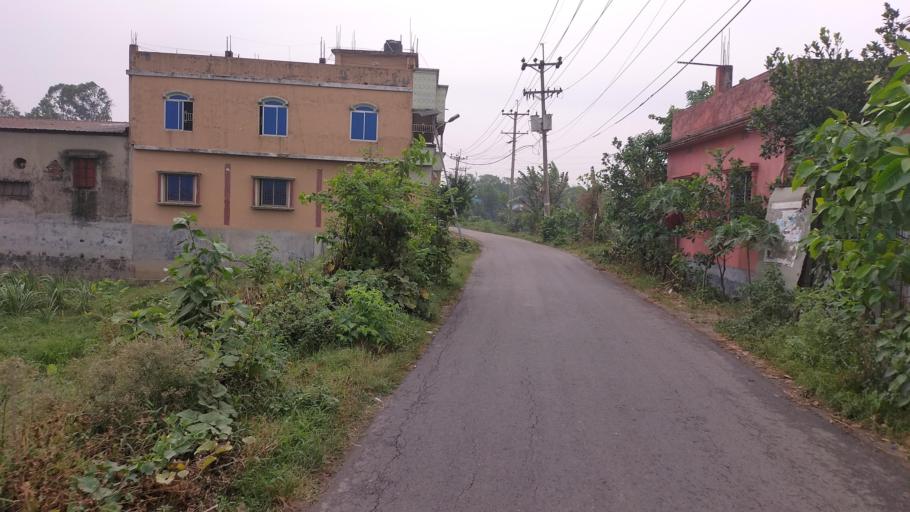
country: BD
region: Dhaka
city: Azimpur
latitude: 23.6803
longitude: 90.3493
